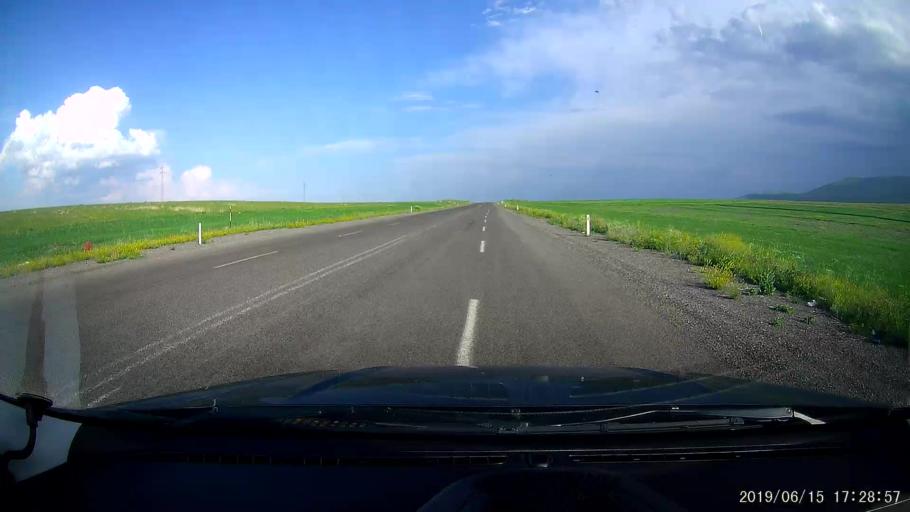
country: TR
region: Kars
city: Basgedikler
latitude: 40.5935
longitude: 43.4471
